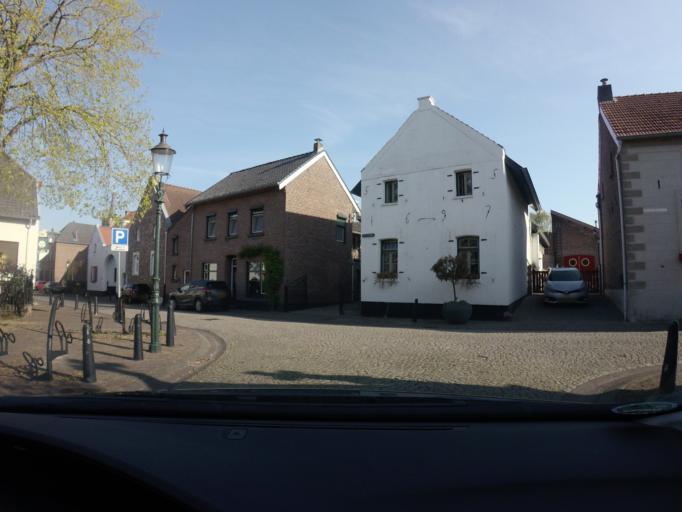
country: NL
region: Limburg
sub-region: Gemeente Stein
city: Elsloo
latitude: 50.9468
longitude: 5.7612
